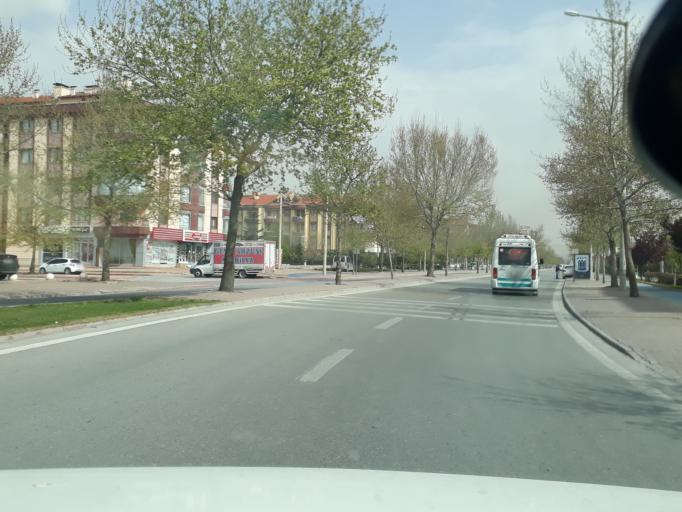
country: TR
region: Konya
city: Selcuklu
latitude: 37.9376
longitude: 32.4932
